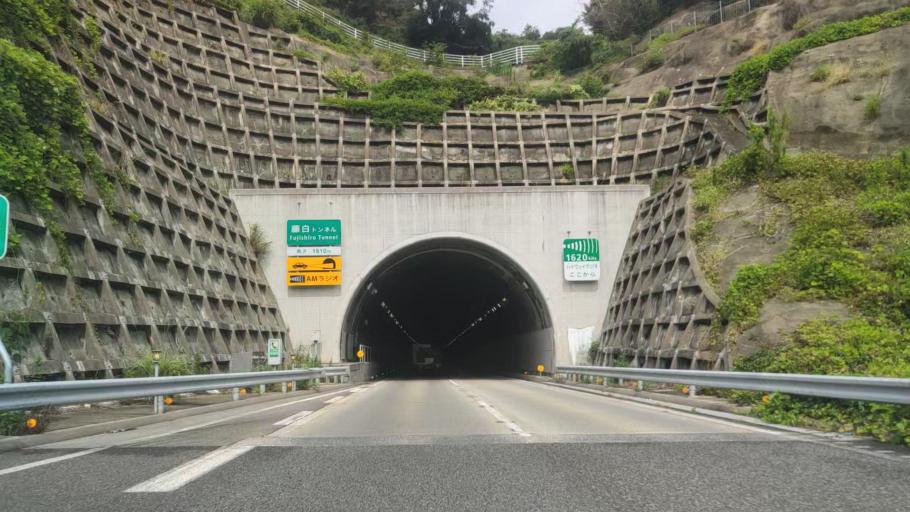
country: JP
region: Wakayama
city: Kainan
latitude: 34.1279
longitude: 135.2012
